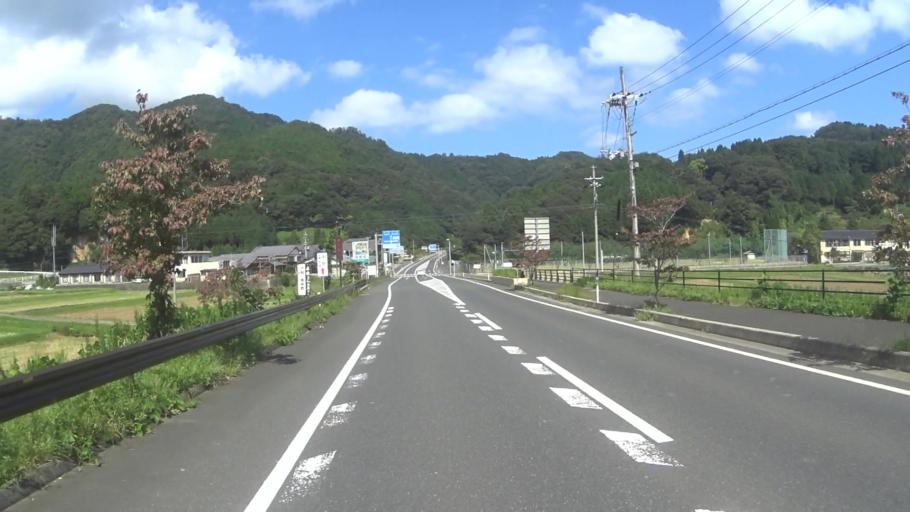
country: JP
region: Kyoto
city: Miyazu
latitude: 35.6727
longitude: 135.2718
